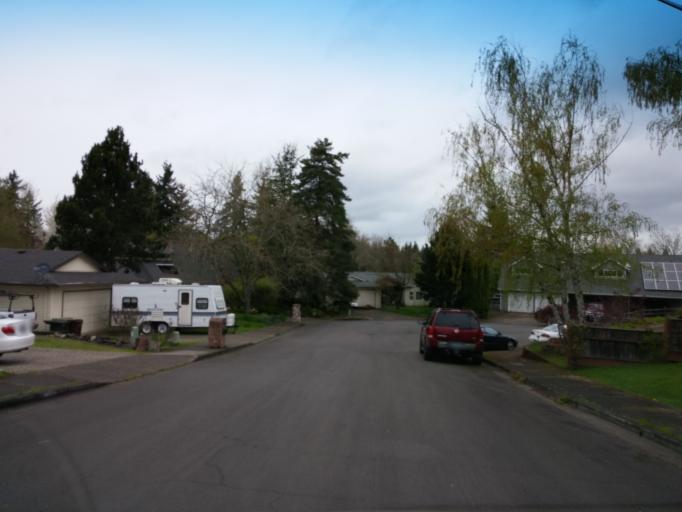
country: US
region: Oregon
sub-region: Washington County
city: Rockcreek
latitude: 45.5298
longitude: -122.8646
